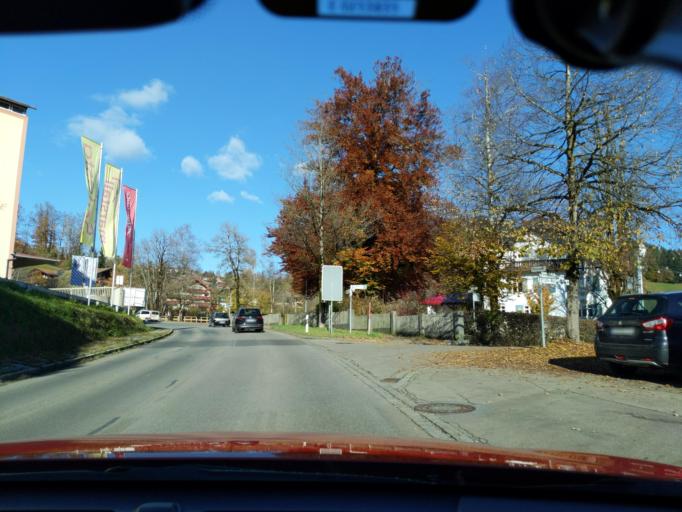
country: DE
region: Bavaria
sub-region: Swabia
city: Oberstaufen
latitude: 47.5447
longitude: 10.0194
